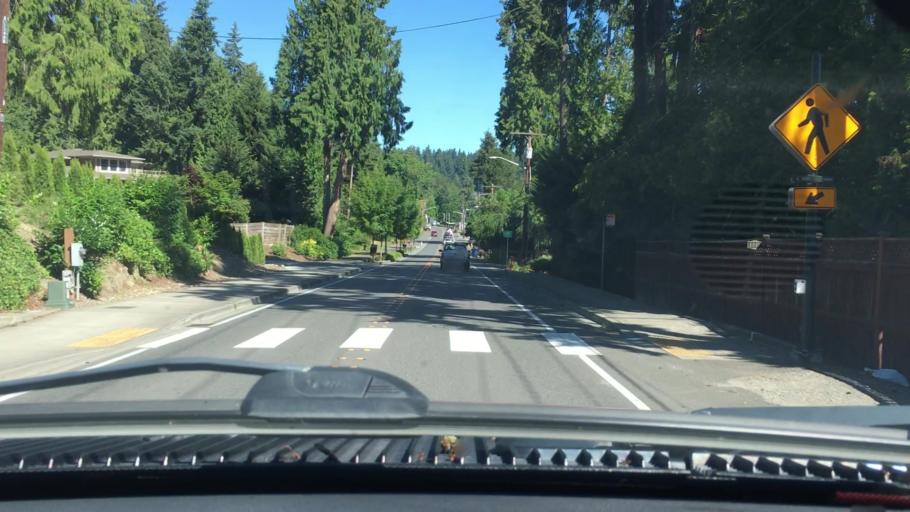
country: US
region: Washington
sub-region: King County
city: West Lake Sammamish
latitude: 47.5729
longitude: -122.1079
